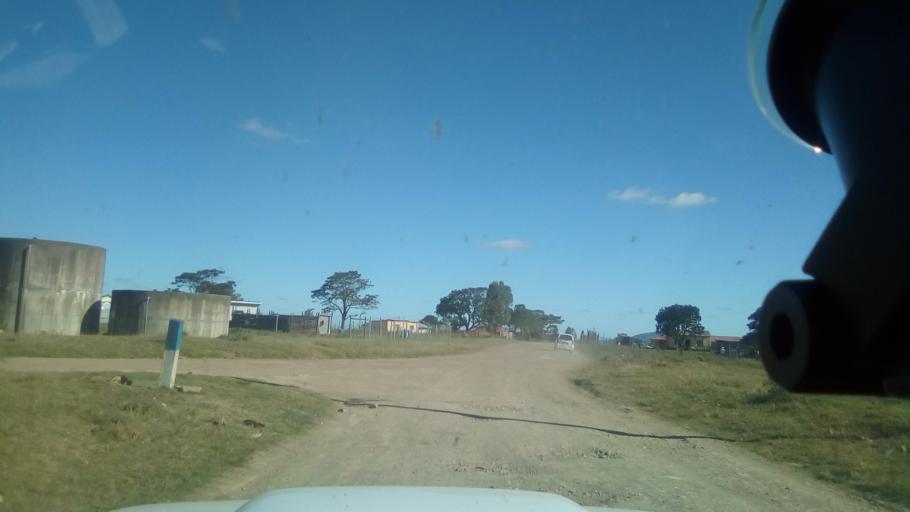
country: ZA
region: Eastern Cape
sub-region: Buffalo City Metropolitan Municipality
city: Bhisho
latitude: -32.7887
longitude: 27.3241
